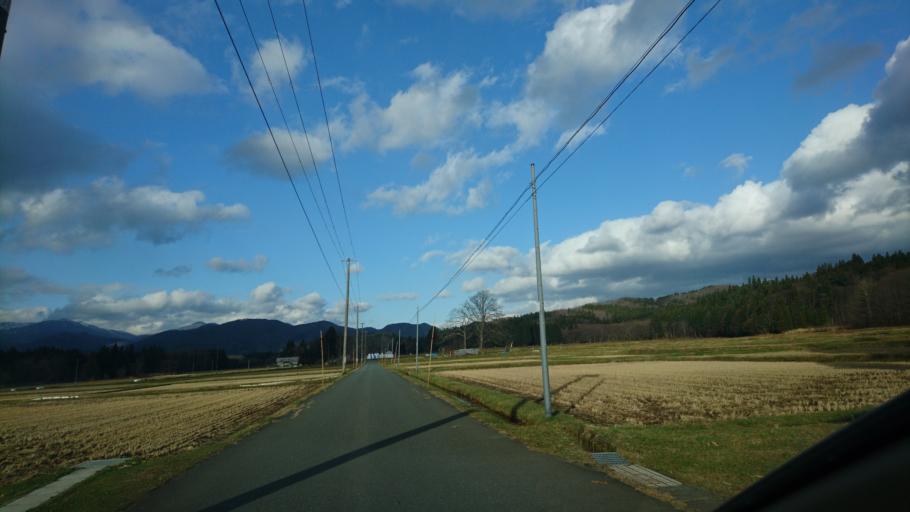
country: JP
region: Akita
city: Kakunodatemachi
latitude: 39.4526
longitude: 140.7842
